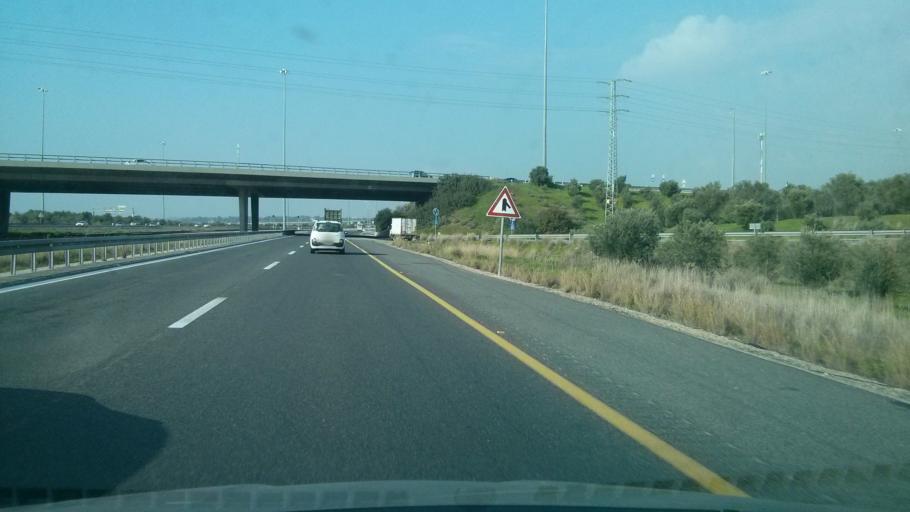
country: IL
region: Central District
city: Gedera
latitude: 31.7932
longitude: 34.8313
